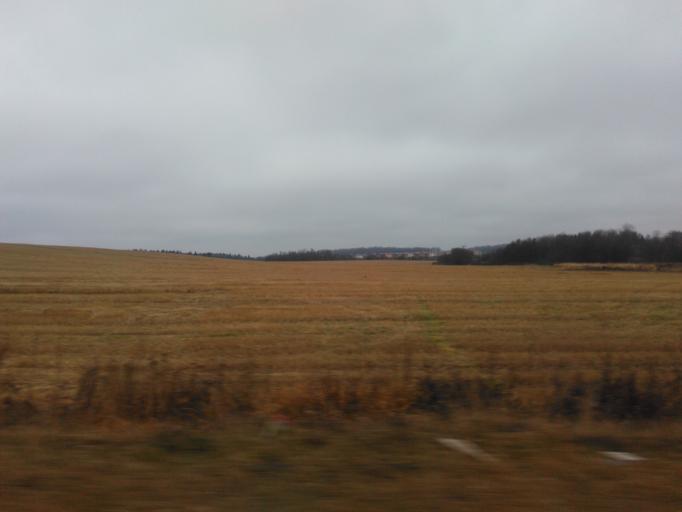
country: RU
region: Moskovskaya
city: Ashukino
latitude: 56.1547
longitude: 37.9794
